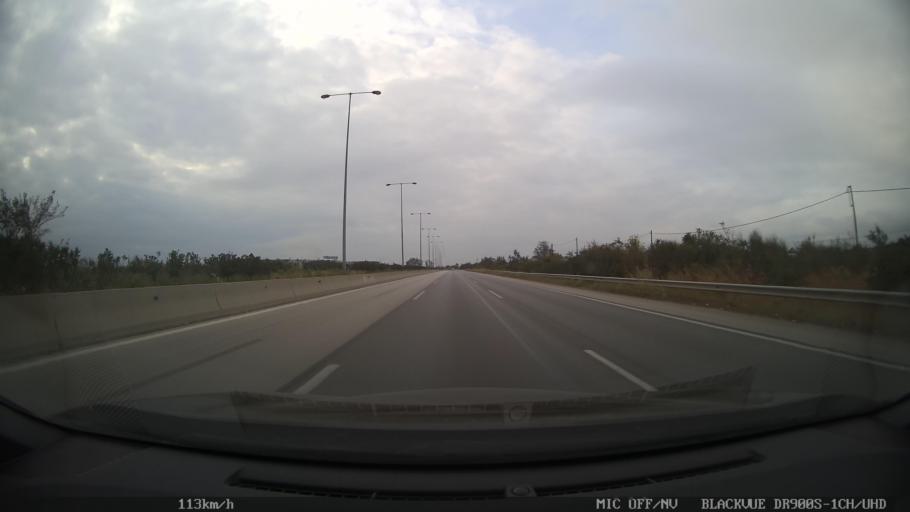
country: GR
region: Central Macedonia
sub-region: Nomos Thessalonikis
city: Nea Magnisia
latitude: 40.6798
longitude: 22.8324
